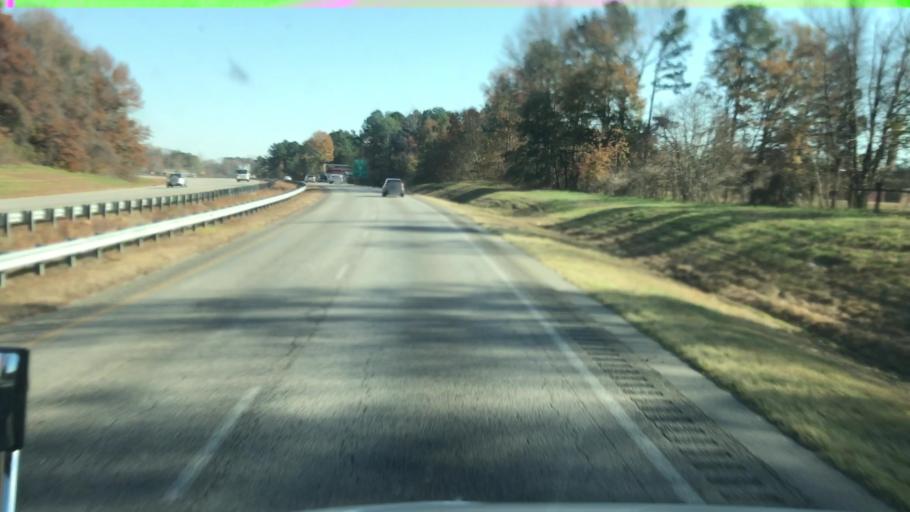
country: US
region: North Carolina
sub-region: Nash County
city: Nashville
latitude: 35.9731
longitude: -77.9450
